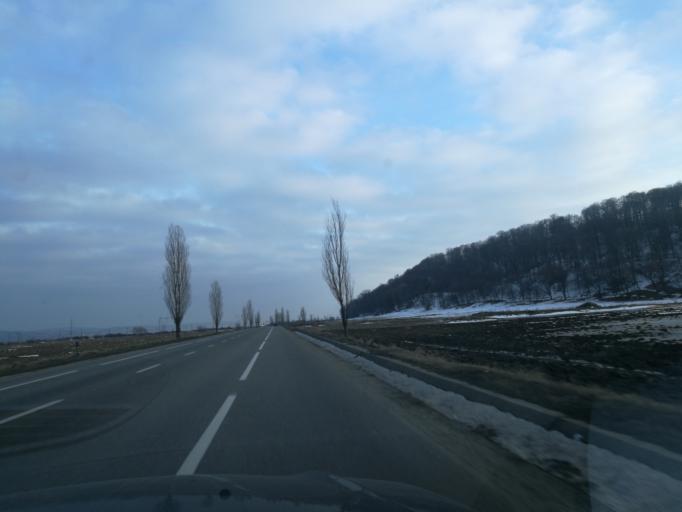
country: RO
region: Bacau
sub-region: Comuna Racaciuni
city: Gheorghe Doja
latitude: 46.3674
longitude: 26.9805
